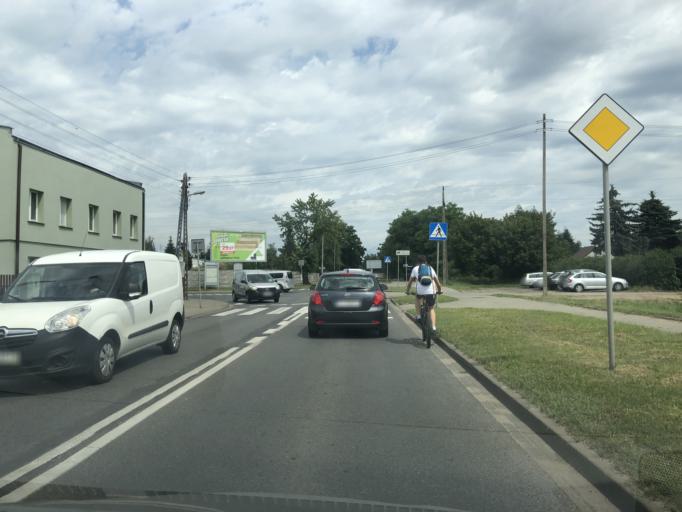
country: PL
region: Greater Poland Voivodeship
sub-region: Powiat poznanski
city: Lubon
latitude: 52.3562
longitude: 16.8844
